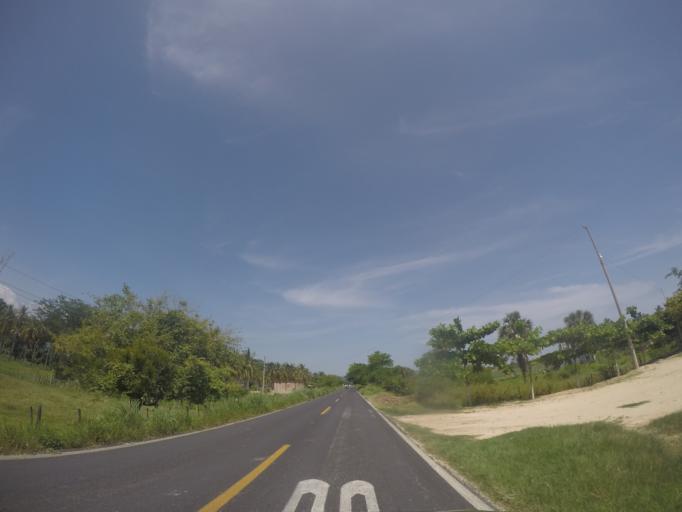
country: MX
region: Oaxaca
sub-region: Villa de Tututepec de Melchor Ocampo
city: Santa Rosa de Lima
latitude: 16.0116
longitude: -97.4569
